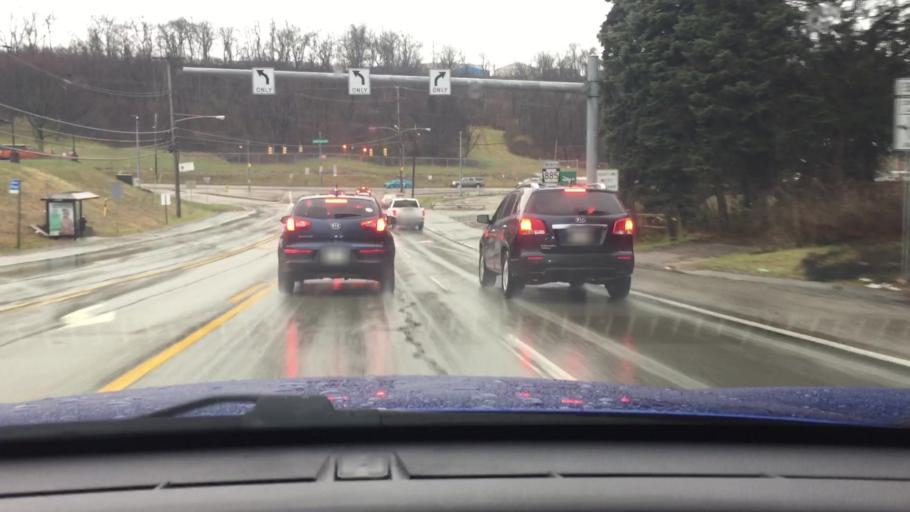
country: US
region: Pennsylvania
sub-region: Allegheny County
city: Pleasant Hills
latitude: 40.3477
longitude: -79.9391
